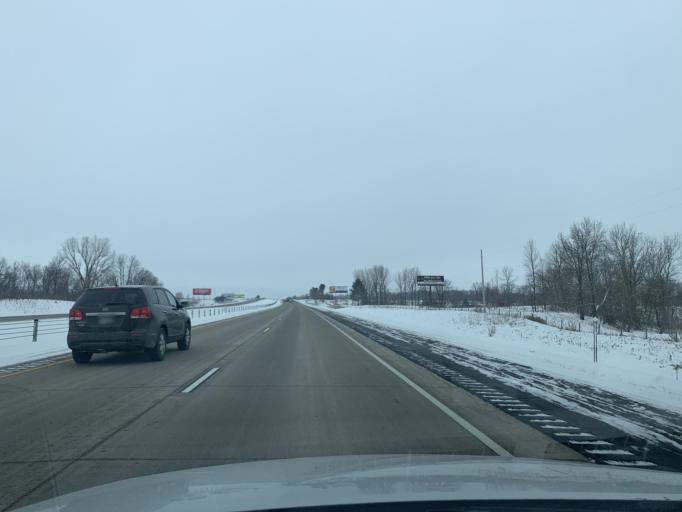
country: US
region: Minnesota
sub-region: Pine County
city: Rock Creek
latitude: 45.7486
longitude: -92.9921
